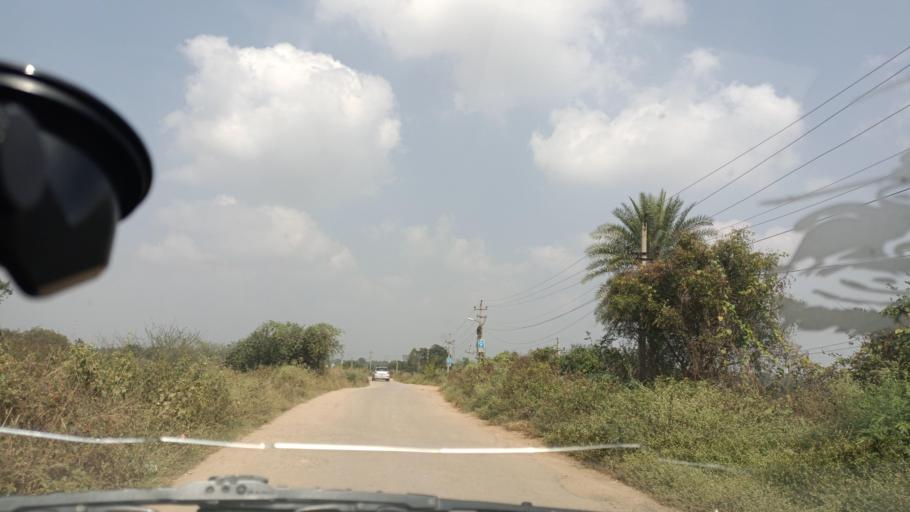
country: IN
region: Karnataka
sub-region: Bangalore Urban
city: Yelahanka
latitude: 13.1763
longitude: 77.6312
